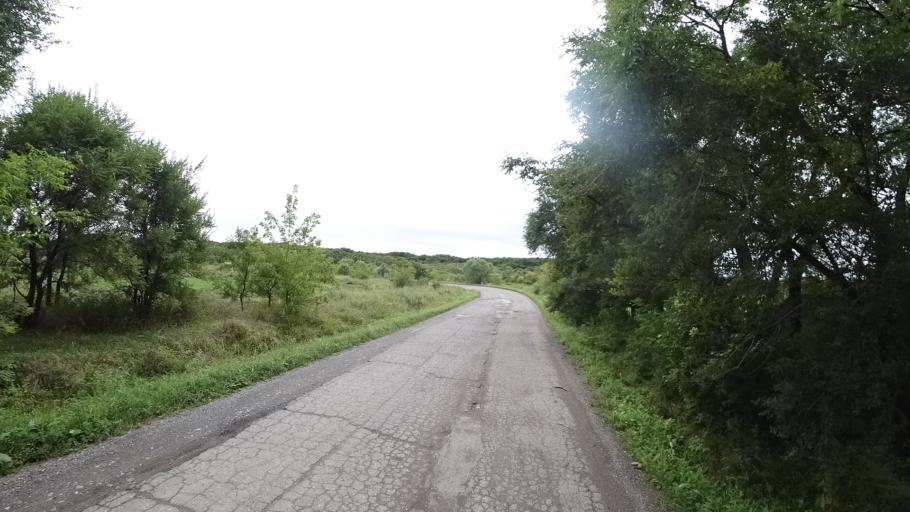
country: RU
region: Primorskiy
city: Lyalichi
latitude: 44.0752
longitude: 132.4761
